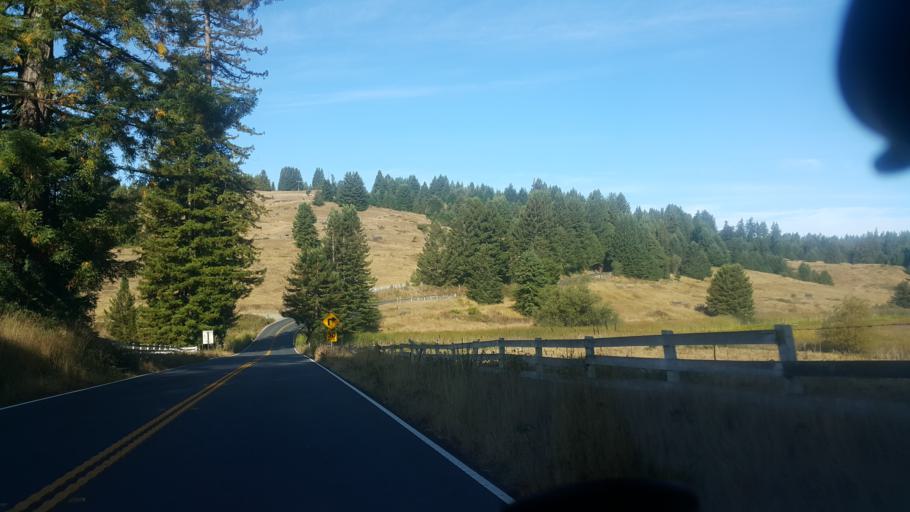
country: US
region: California
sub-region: Mendocino County
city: Fort Bragg
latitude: 39.3538
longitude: -123.6123
